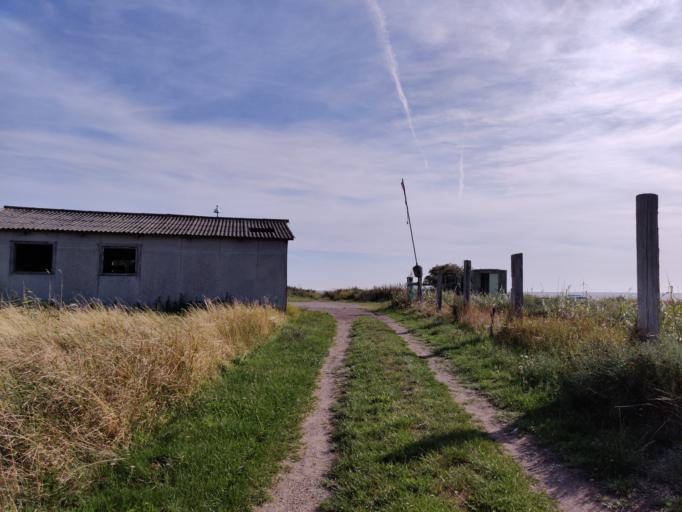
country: DK
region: Zealand
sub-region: Guldborgsund Kommune
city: Nykobing Falster
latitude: 54.6610
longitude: 11.8679
